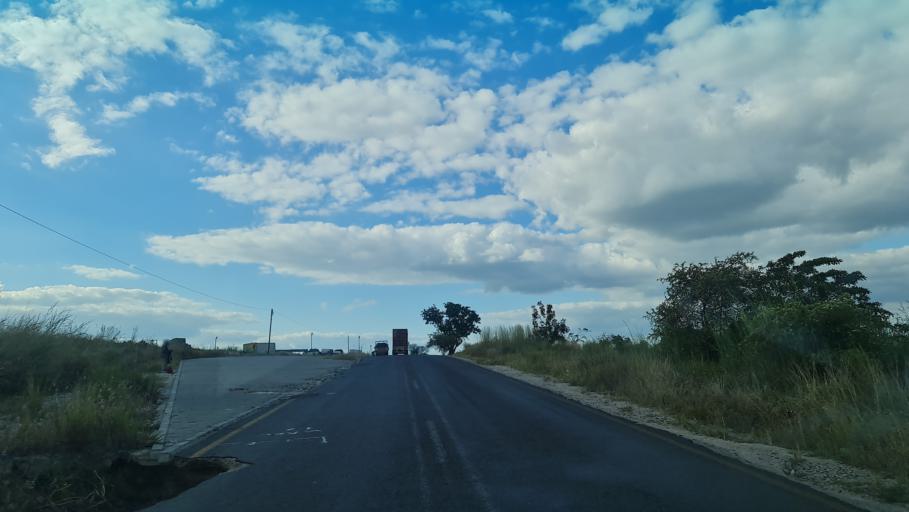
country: MZ
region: Manica
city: Chimoio
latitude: -19.2212
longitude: 33.9212
